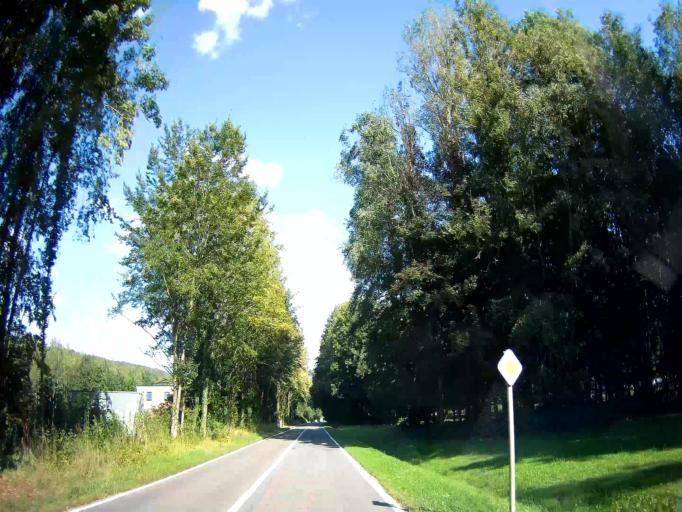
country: BE
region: Wallonia
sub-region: Province de Namur
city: Anhee
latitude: 50.3172
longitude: 4.8445
